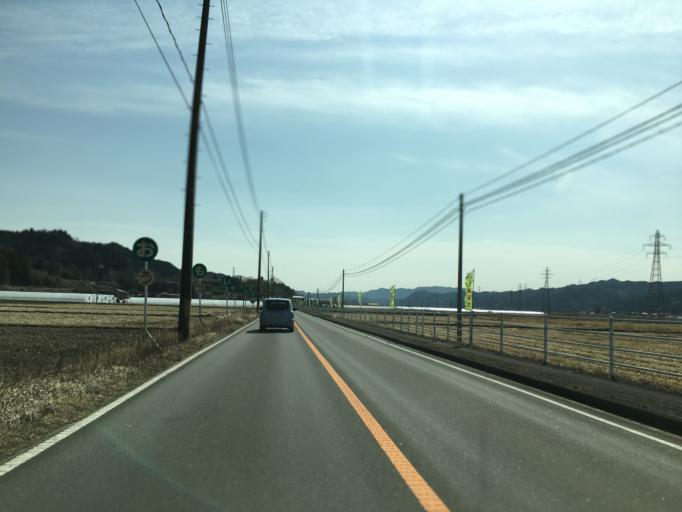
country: JP
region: Ibaraki
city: Daigo
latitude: 36.9221
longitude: 140.4156
